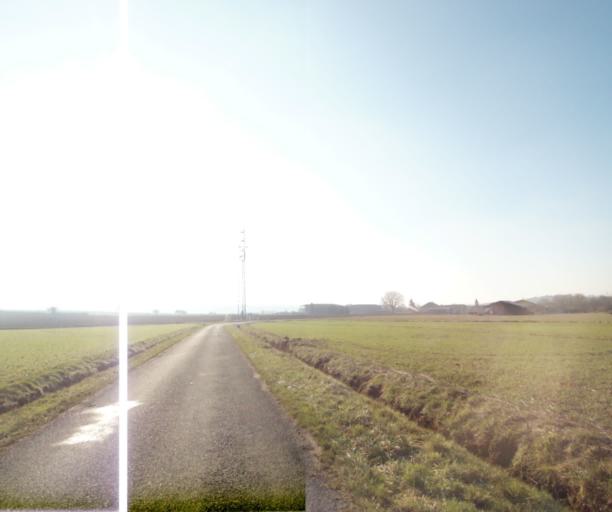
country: FR
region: Champagne-Ardenne
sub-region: Departement de la Haute-Marne
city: Bienville
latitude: 48.5434
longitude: 5.0282
